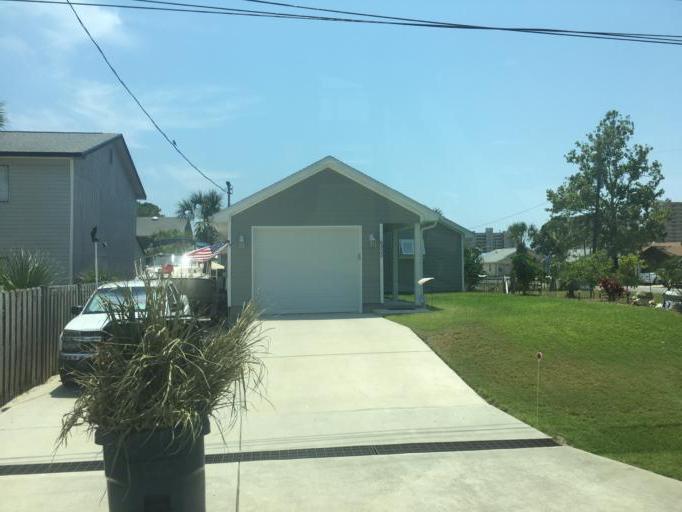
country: US
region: Florida
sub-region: Bay County
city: Lower Grand Lagoon
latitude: 30.1540
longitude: -85.7632
